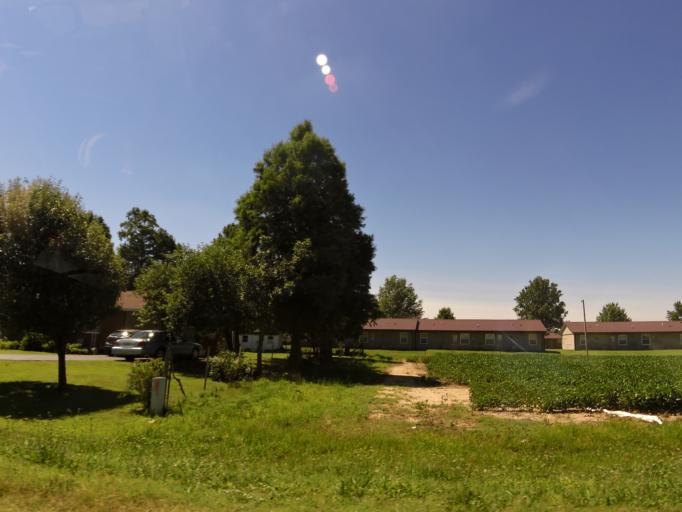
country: US
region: Missouri
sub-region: New Madrid County
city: Lilbourn
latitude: 36.5672
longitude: -89.6028
